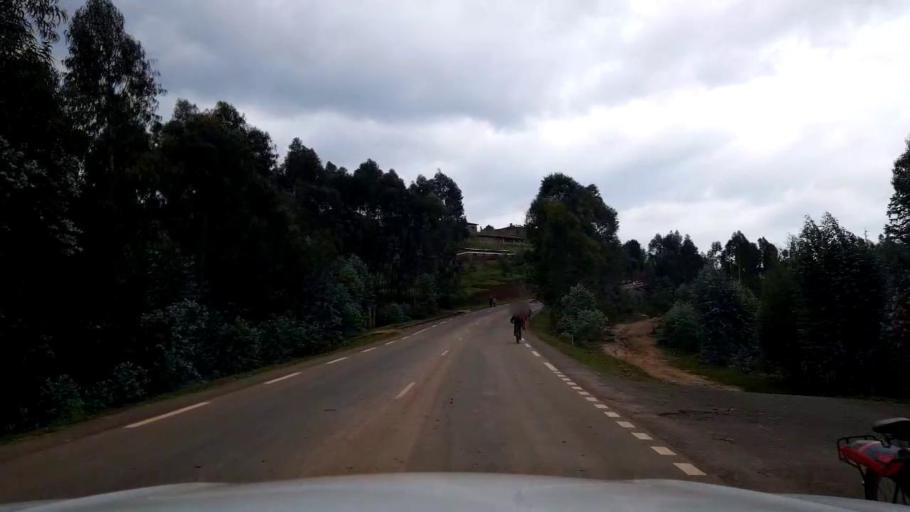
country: RW
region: Western Province
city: Kibuye
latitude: -1.8801
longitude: 29.3512
